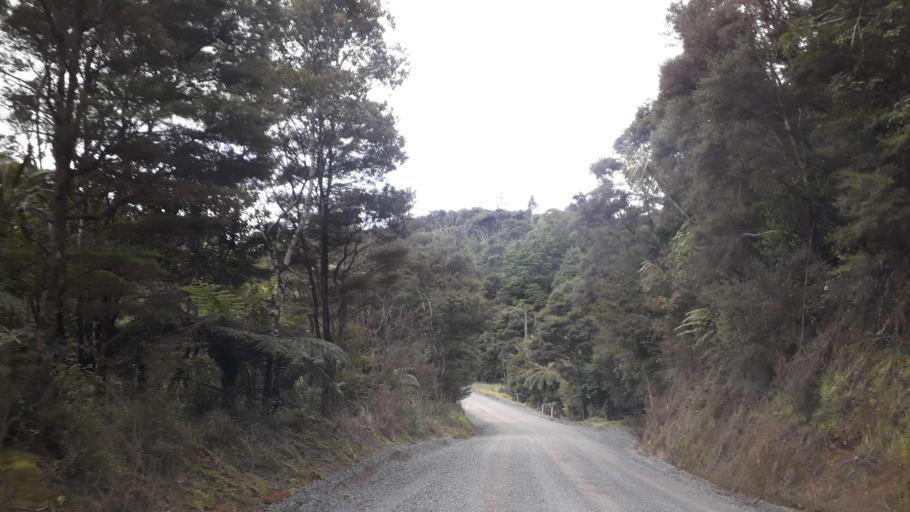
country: NZ
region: Northland
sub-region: Far North District
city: Paihia
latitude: -35.3209
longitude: 174.2337
